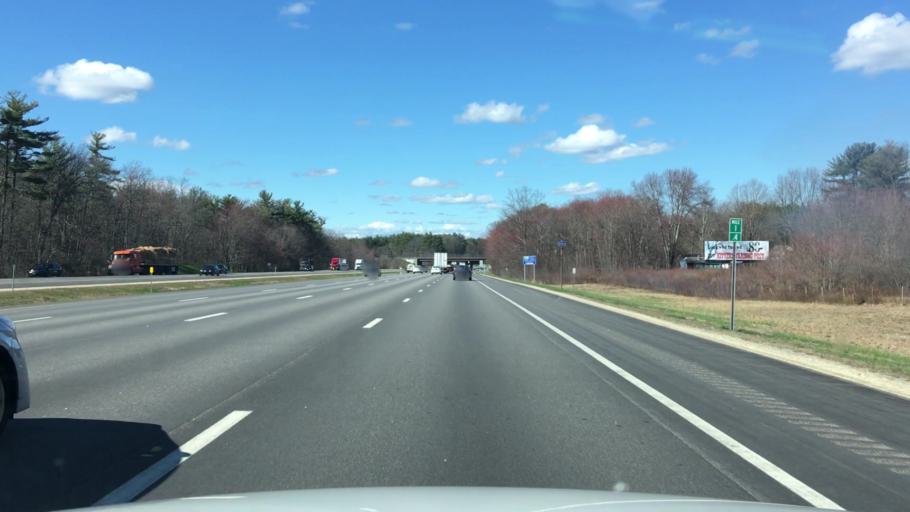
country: US
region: New Hampshire
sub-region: Rockingham County
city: Seabrook
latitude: 42.9010
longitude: -70.8782
